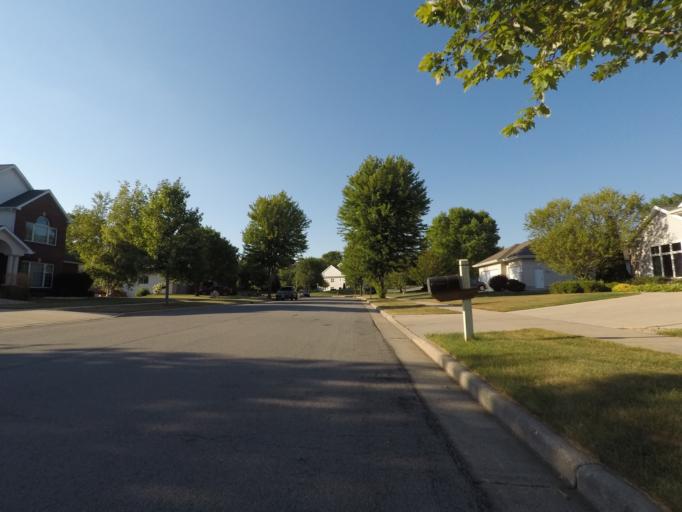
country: US
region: Wisconsin
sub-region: Dane County
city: Verona
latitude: 43.0044
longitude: -89.5352
